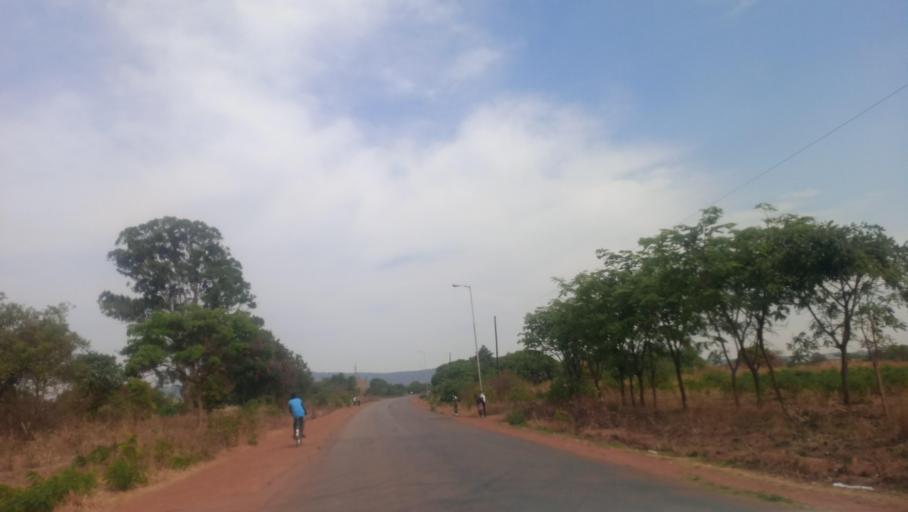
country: ZM
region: Northern
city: Mpika
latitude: -11.8338
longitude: 31.4243
